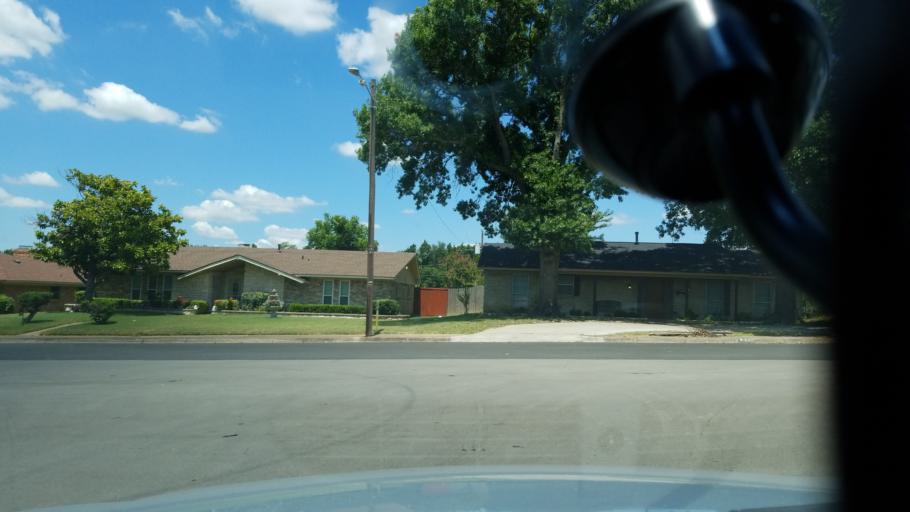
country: US
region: Texas
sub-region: Dallas County
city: Duncanville
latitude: 32.6691
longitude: -96.8620
